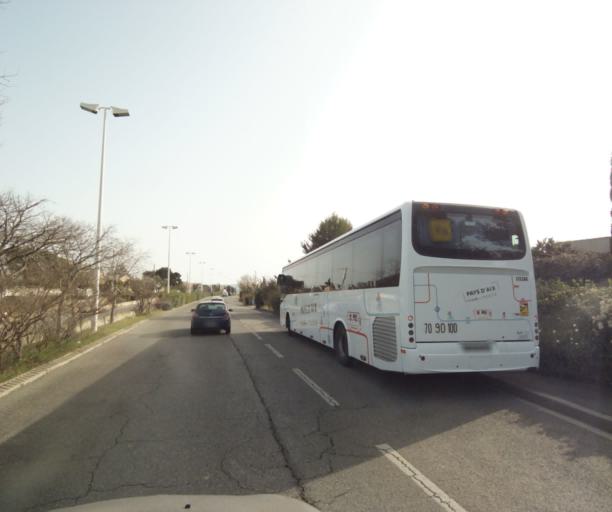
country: FR
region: Provence-Alpes-Cote d'Azur
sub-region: Departement des Bouches-du-Rhone
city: Vitrolles
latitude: 43.4537
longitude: 5.2436
